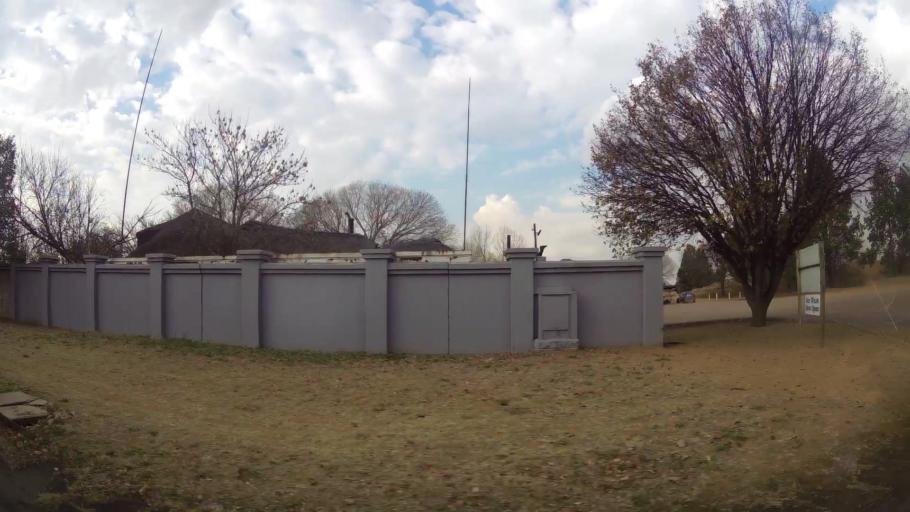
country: ZA
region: Orange Free State
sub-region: Fezile Dabi District Municipality
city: Sasolburg
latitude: -26.7913
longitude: 27.8228
